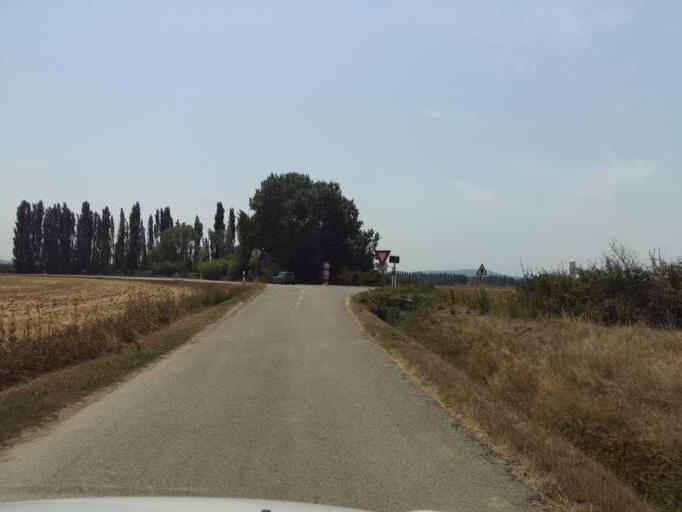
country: FR
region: Languedoc-Roussillon
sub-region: Departement du Gard
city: Pont-Saint-Esprit
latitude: 44.2569
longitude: 4.6801
